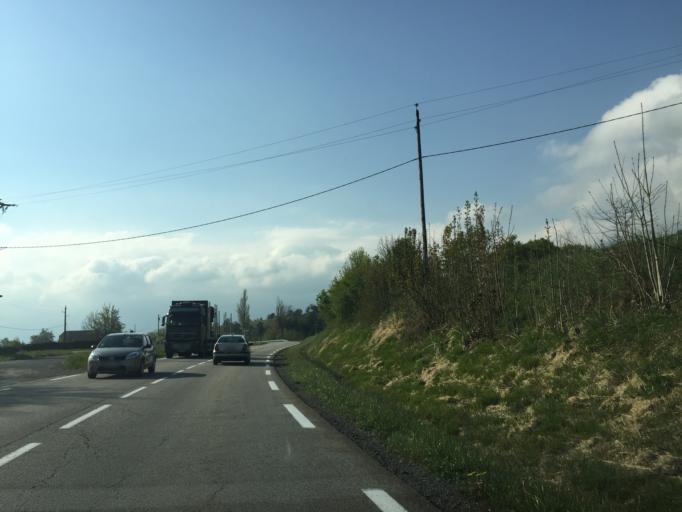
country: FR
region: Rhone-Alpes
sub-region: Departement de l'Isere
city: Mens
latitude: 44.8211
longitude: 5.6249
